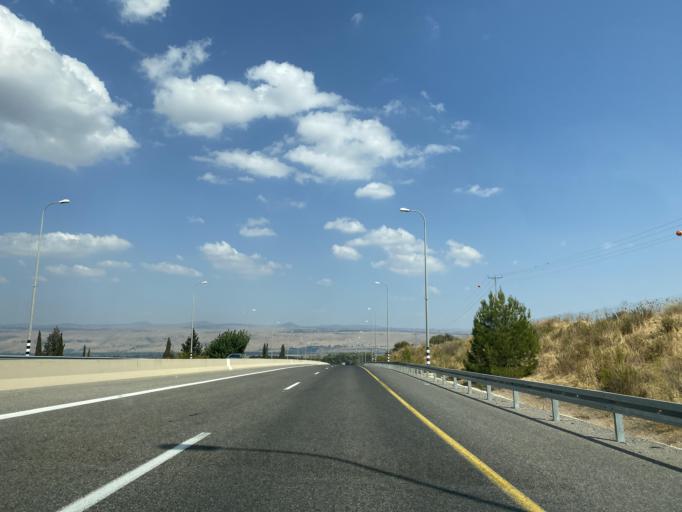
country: IL
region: Northern District
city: Rosh Pinna
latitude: 33.0278
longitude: 35.5608
